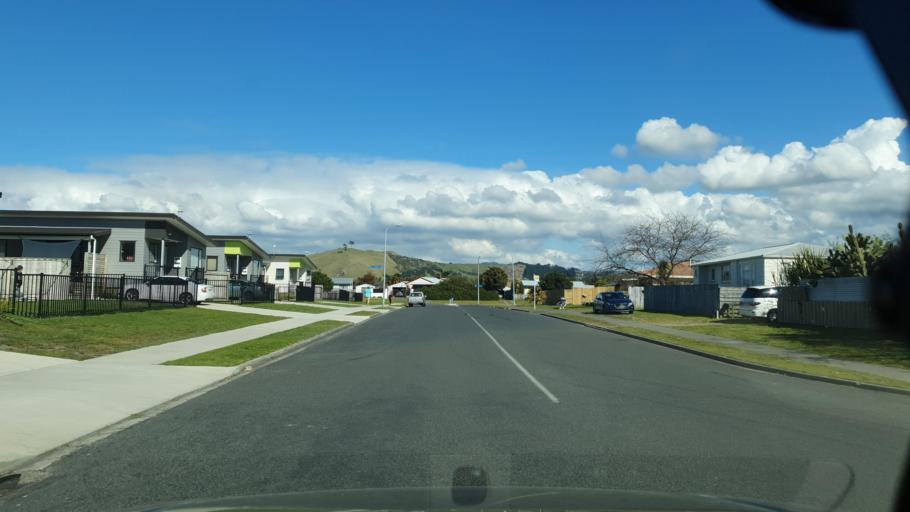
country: NZ
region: Bay of Plenty
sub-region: Tauranga City
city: Tauranga
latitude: -37.7061
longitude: 176.2908
